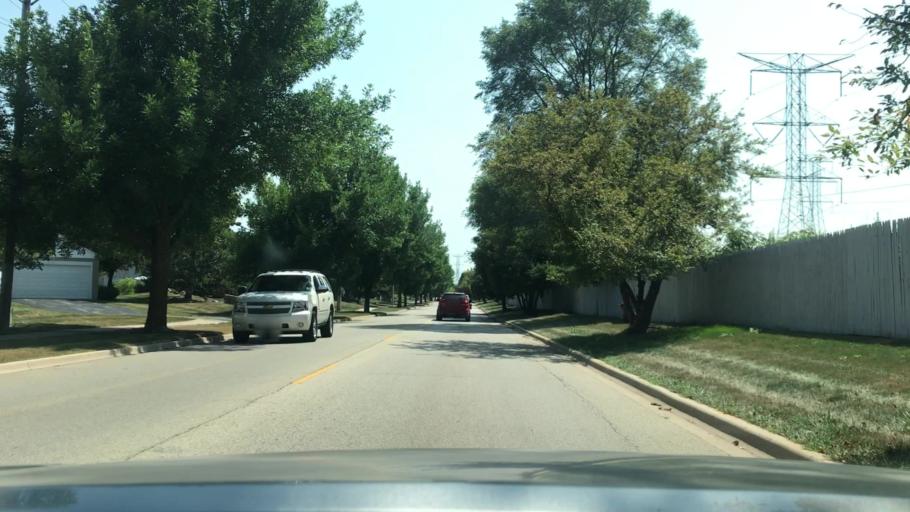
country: US
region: Illinois
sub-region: Kane County
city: Aurora
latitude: 41.7288
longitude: -88.2349
